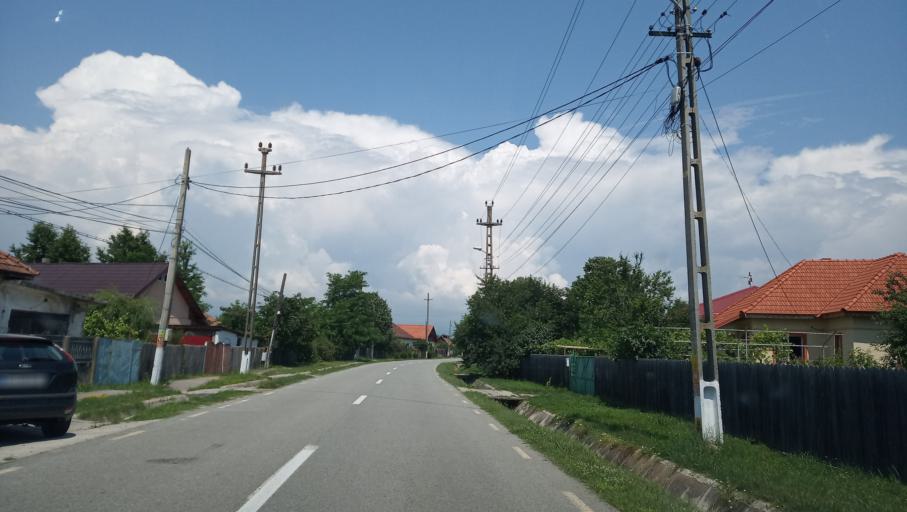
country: RO
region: Gorj
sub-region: Comuna Turcinesti
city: Turcinesti
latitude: 45.0650
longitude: 23.3478
